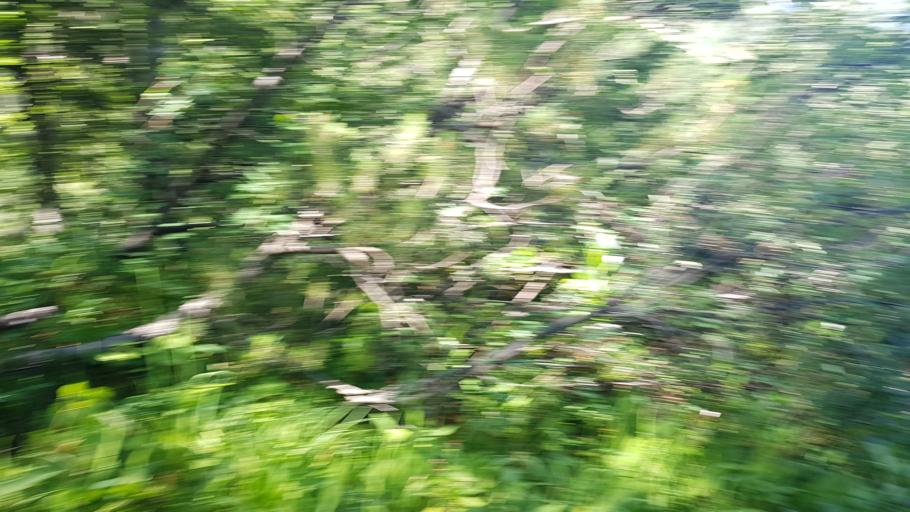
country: IT
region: Friuli Venezia Giulia
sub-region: Provincia di Udine
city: Paularo
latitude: 46.4756
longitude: 13.1632
